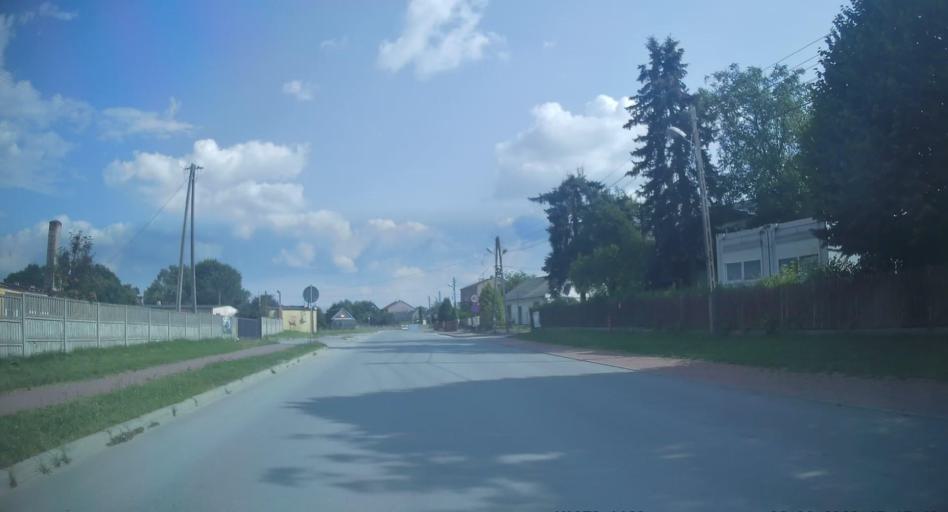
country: PL
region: Swietokrzyskie
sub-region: Powiat konecki
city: Radoszyce
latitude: 51.0777
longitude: 20.2564
